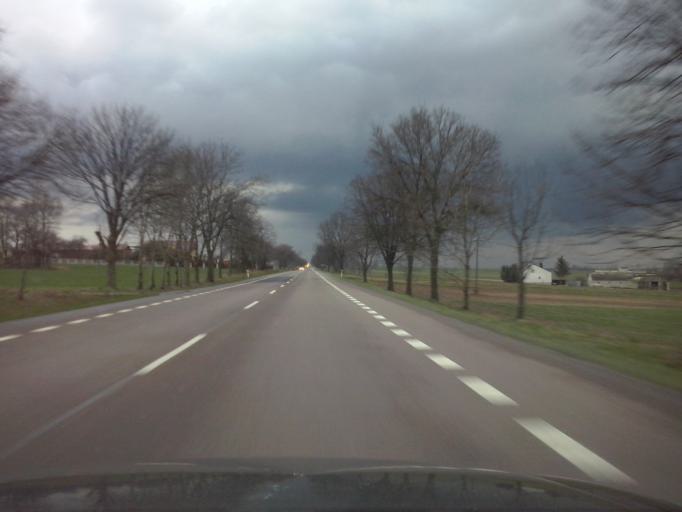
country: PL
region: Lublin Voivodeship
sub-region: Powiat chelmski
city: Rejowiec Fabryczny
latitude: 51.1763
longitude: 23.2388
